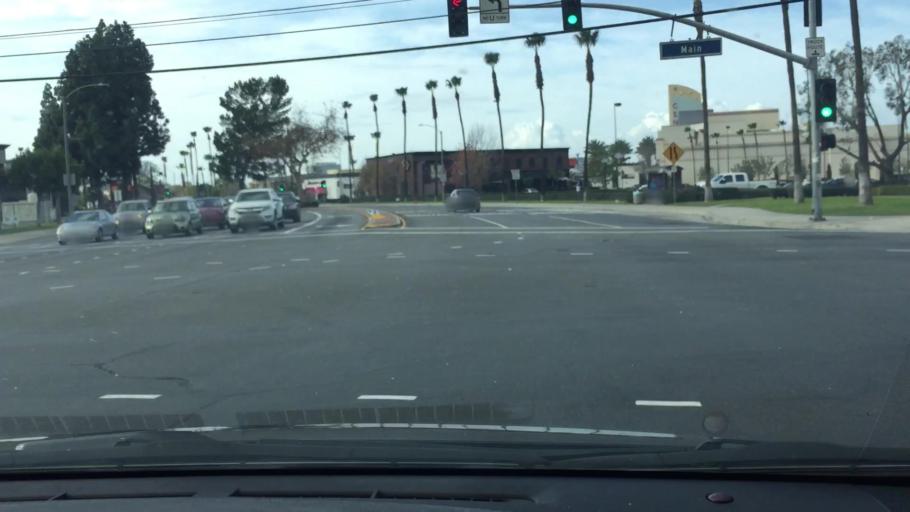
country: US
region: California
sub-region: Orange County
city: Orange
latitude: 33.8090
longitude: -117.8670
